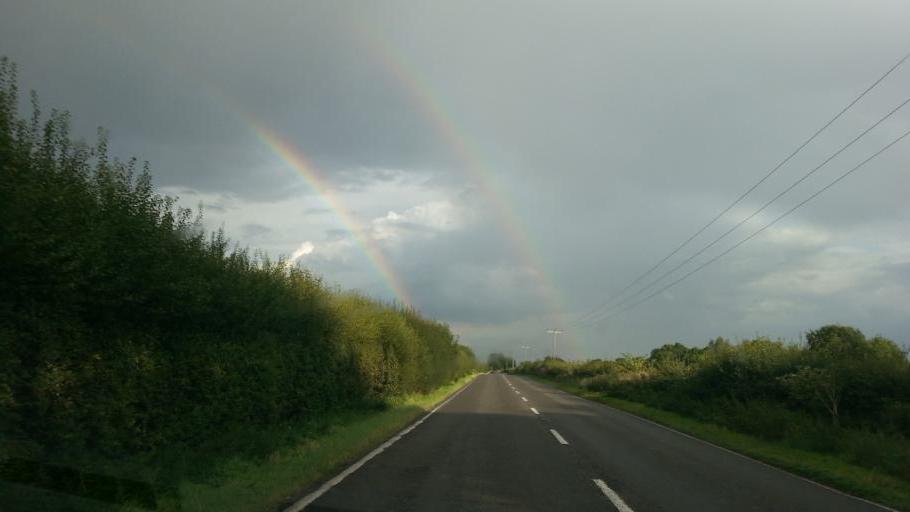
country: GB
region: England
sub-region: Nottinghamshire
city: Southwell
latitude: 53.1111
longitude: -0.9671
